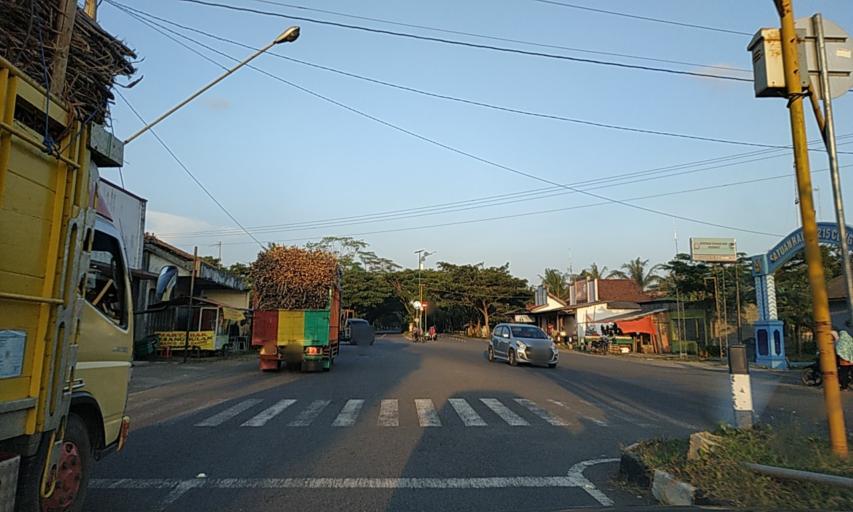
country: ID
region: Central Java
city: Kutoarjo
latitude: -7.8853
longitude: 110.0426
